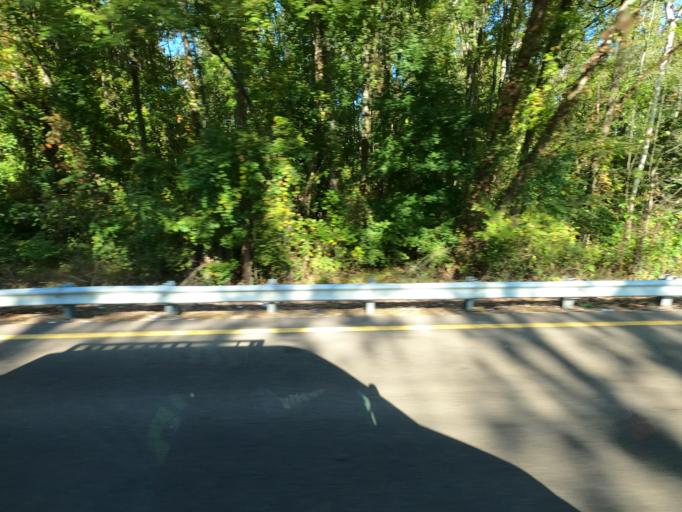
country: US
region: Tennessee
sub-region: Tipton County
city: Atoka
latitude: 35.4380
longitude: -89.7968
